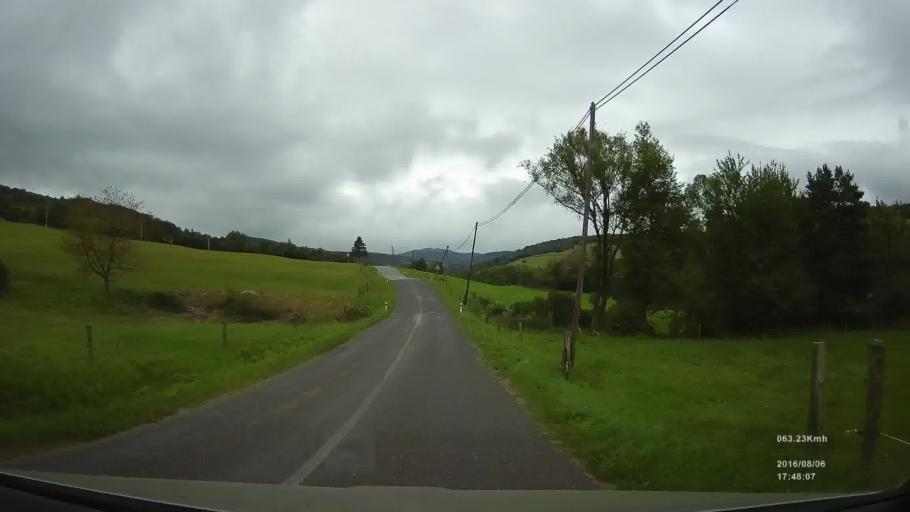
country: SK
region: Presovsky
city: Svidnik
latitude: 49.3745
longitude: 21.5744
